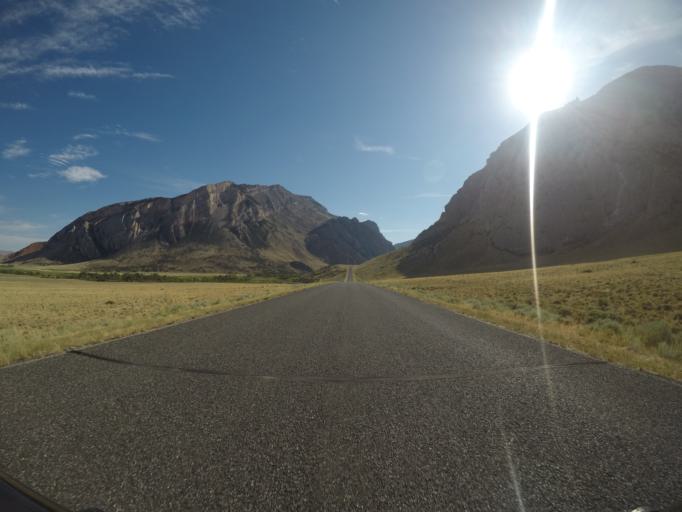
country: US
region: Montana
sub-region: Carbon County
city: Red Lodge
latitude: 44.8584
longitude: -109.2920
